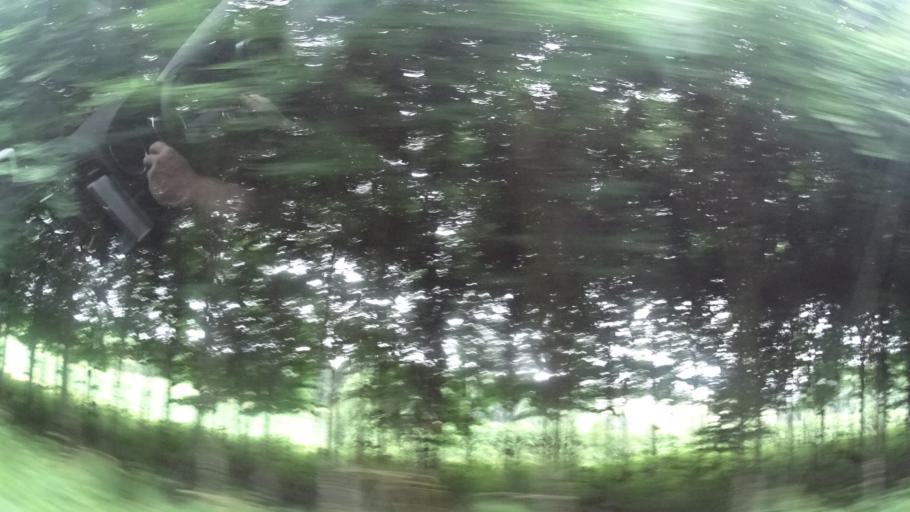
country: BE
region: Wallonia
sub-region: Province du Luxembourg
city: Aubange
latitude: 49.5992
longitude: 5.7712
